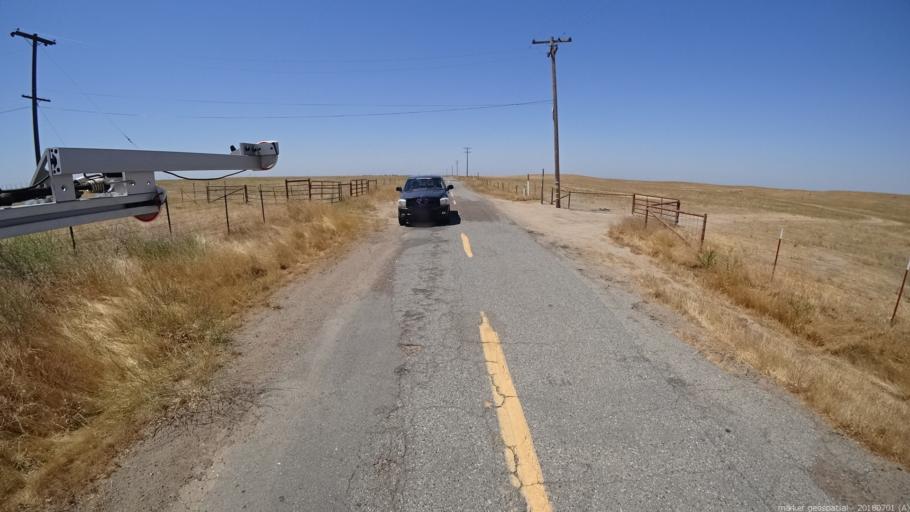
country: US
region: California
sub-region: Madera County
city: Madera Acres
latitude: 37.1096
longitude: -119.9911
